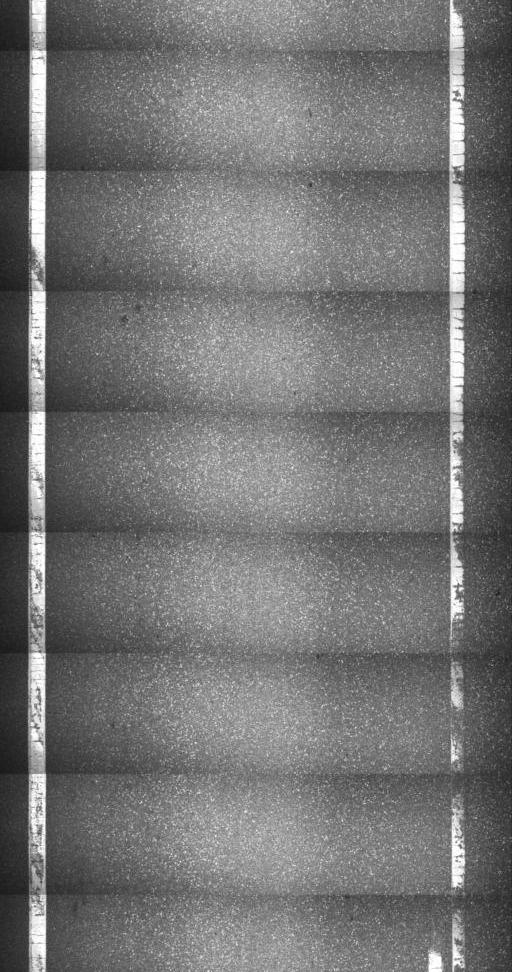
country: US
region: Vermont
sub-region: Orange County
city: Chelsea
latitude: 43.9811
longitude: -72.3594
